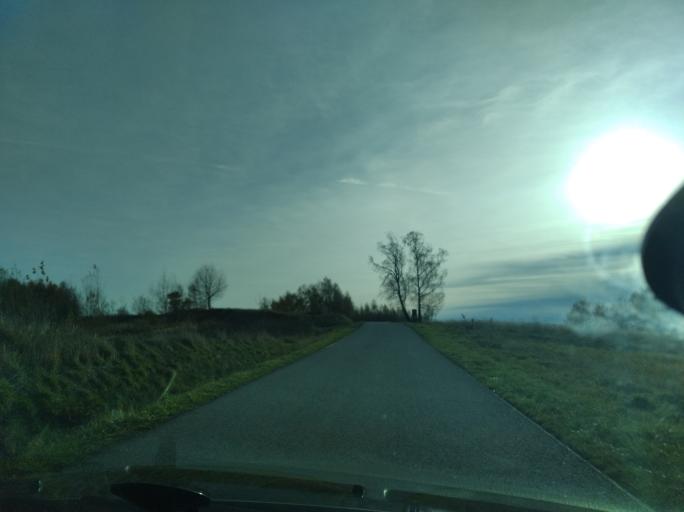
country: PL
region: Subcarpathian Voivodeship
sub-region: Powiat rzeszowski
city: Siedliska
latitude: 49.9353
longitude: 21.9592
